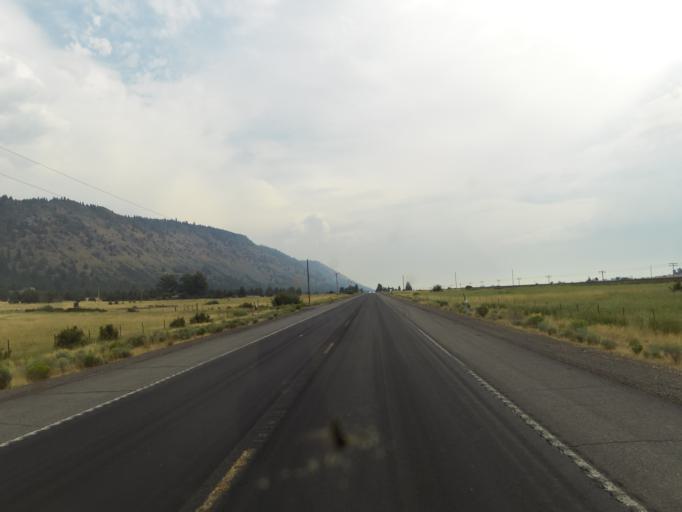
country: US
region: Oregon
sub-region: Klamath County
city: Klamath Falls
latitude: 42.4823
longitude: -121.8754
